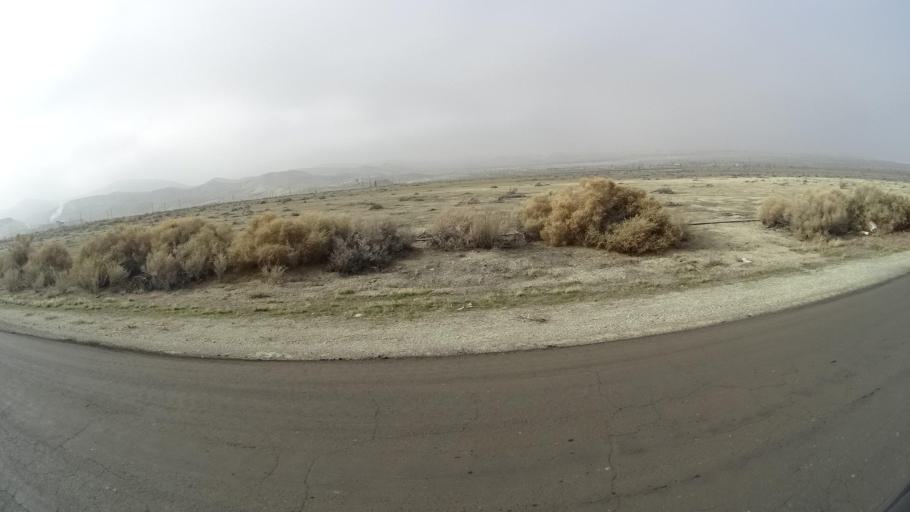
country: US
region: California
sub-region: Kern County
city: Maricopa
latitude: 35.0392
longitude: -119.3670
